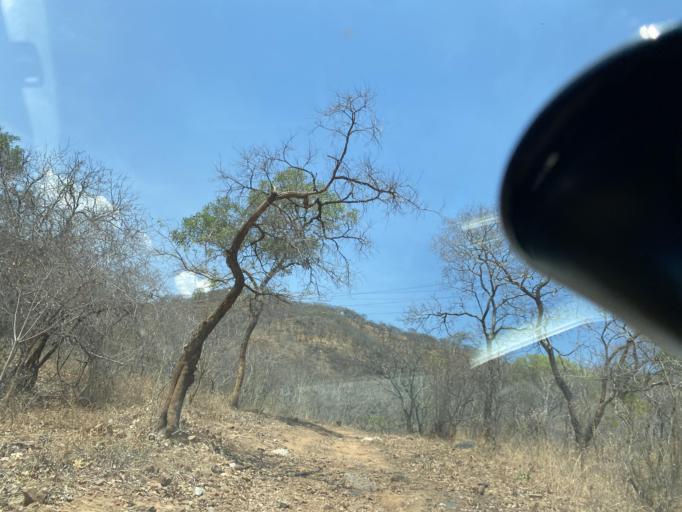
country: ZM
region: Lusaka
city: Kafue
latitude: -15.7437
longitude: 28.4714
